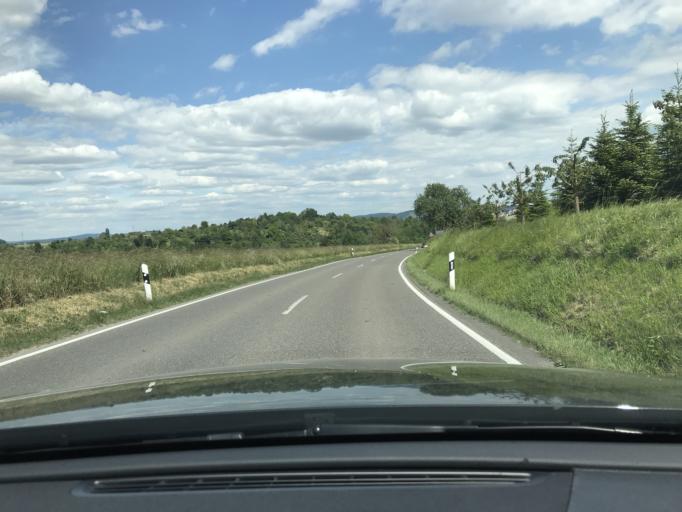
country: DE
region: Baden-Wuerttemberg
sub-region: Regierungsbezirk Stuttgart
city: Schwaikheim
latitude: 48.8735
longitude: 9.3211
